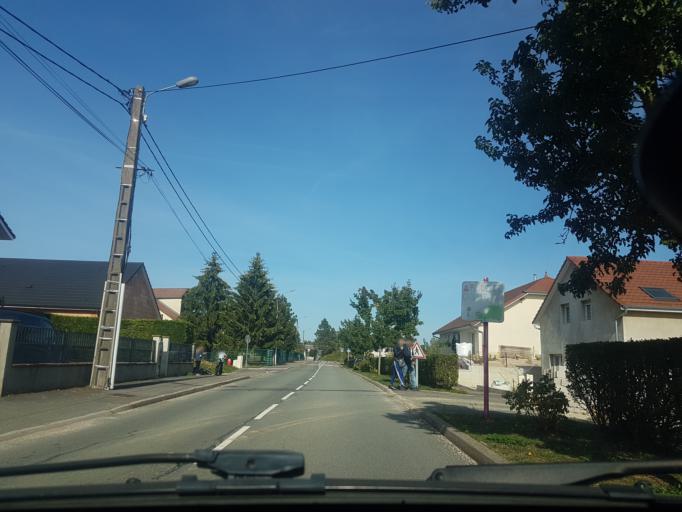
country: FR
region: Franche-Comte
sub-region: Territoire de Belfort
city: Offemont
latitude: 47.6569
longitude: 6.9049
